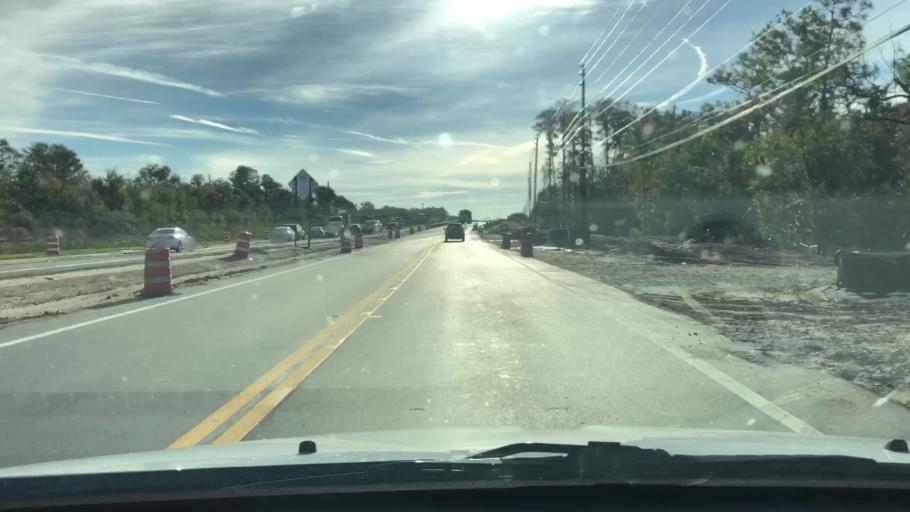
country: US
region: Florida
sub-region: Orange County
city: Meadow Woods
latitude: 28.3929
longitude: -81.3240
